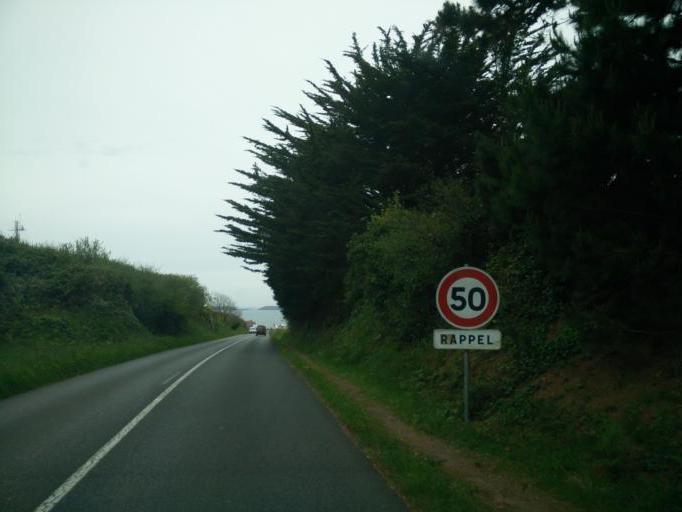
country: FR
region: Brittany
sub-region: Departement des Cotes-d'Armor
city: Tregastel
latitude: 48.8241
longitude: -3.4717
